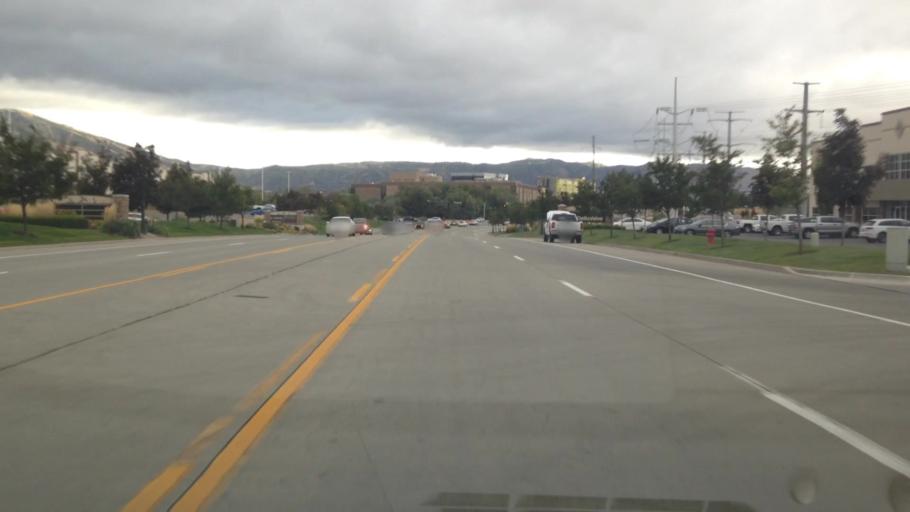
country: US
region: Utah
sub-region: Salt Lake County
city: South Jordan
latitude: 40.5721
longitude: -111.9058
